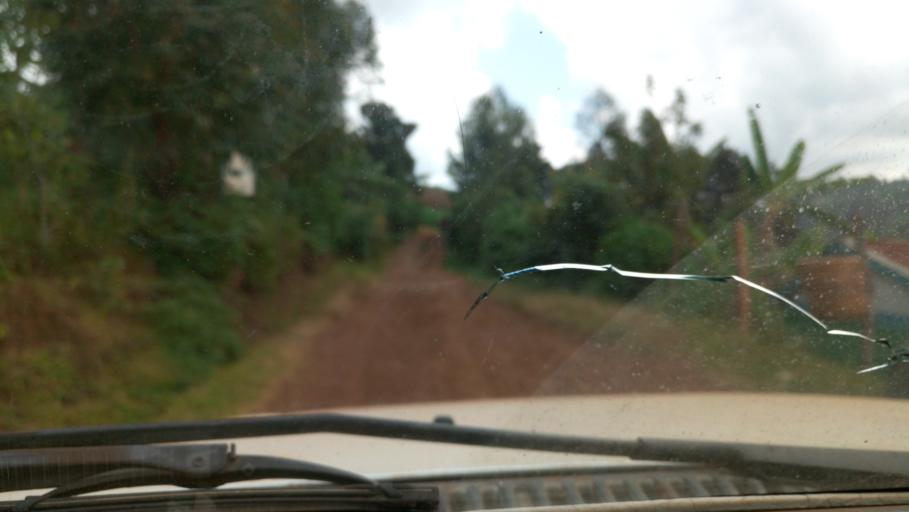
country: KE
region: Murang'a District
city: Kangema
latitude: -0.7627
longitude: 36.9245
